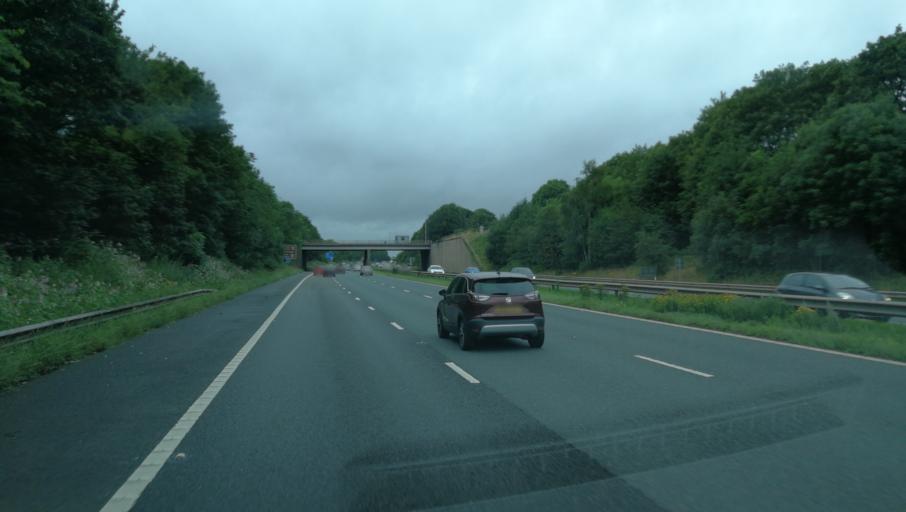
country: GB
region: England
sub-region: Borough of Wigan
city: Tyldesley
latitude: 53.5482
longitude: -2.4660
